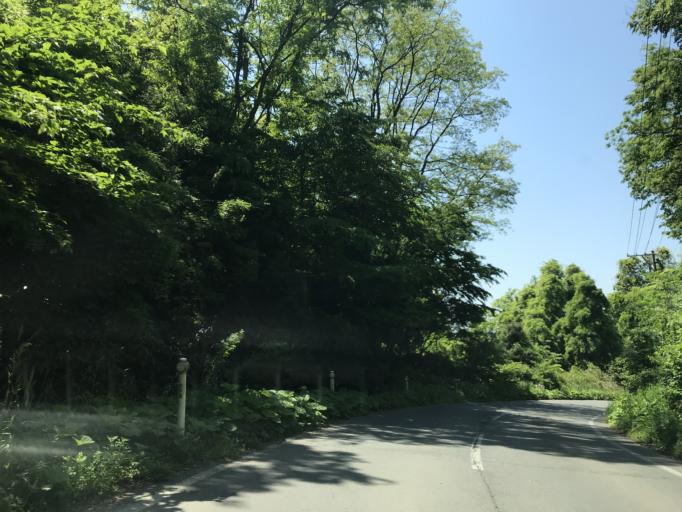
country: JP
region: Iwate
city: Mizusawa
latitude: 39.1629
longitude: 141.0665
